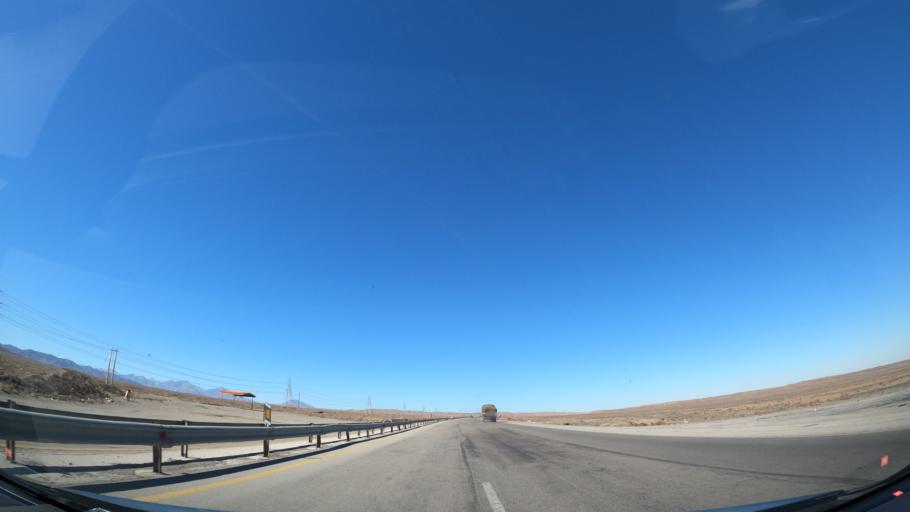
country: IR
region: Isfahan
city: Kashan
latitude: 33.7588
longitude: 51.6747
